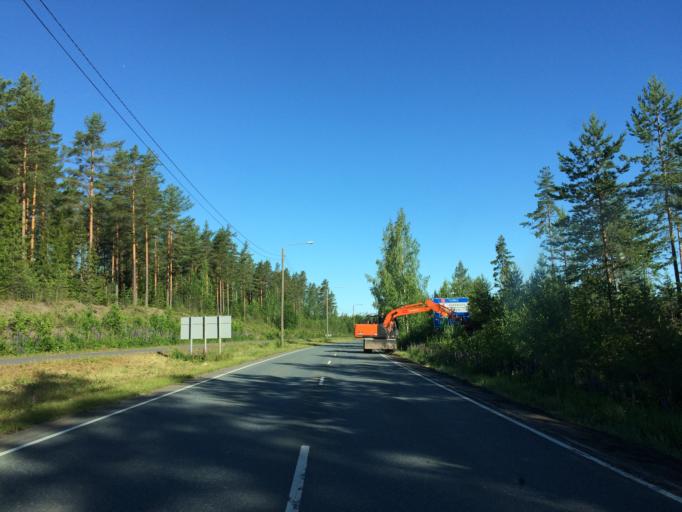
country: FI
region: Haeme
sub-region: Haemeenlinna
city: Haemeenlinna
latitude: 60.9610
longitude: 24.4552
